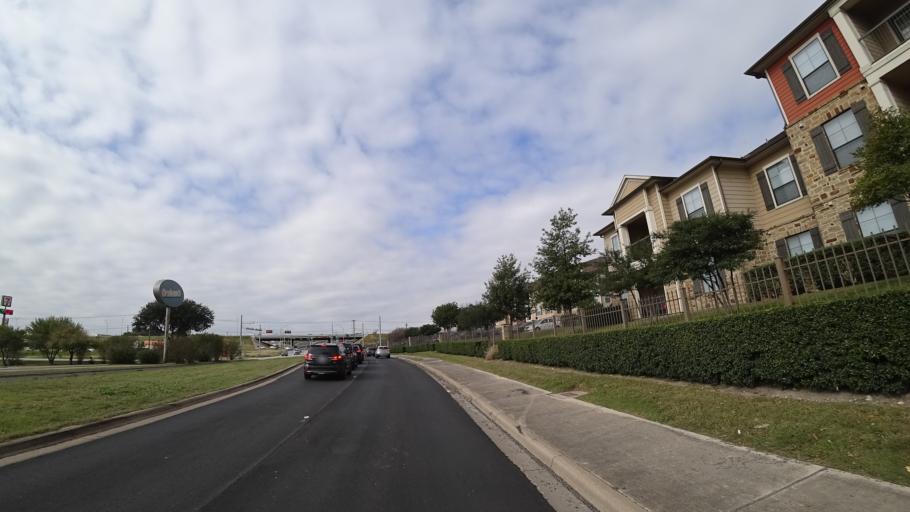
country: US
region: Texas
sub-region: Travis County
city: Windemere
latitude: 30.4564
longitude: -97.6634
